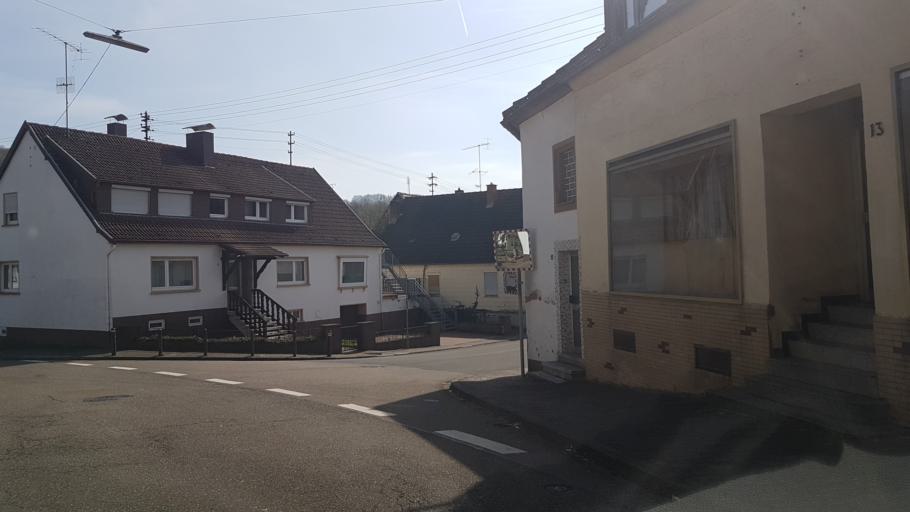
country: DE
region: Rheinland-Pfalz
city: Altenkirchen
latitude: 49.4422
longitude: 7.3217
